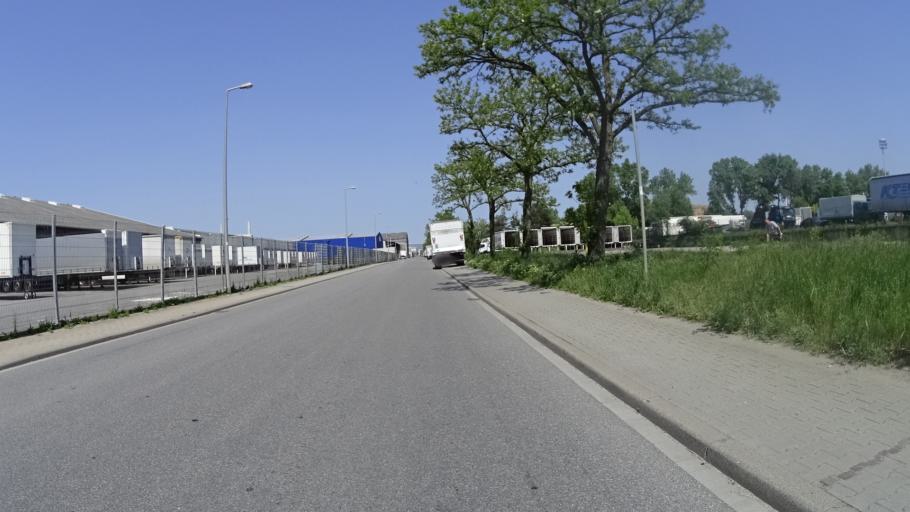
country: DE
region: Rheinland-Pfalz
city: Altrip
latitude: 49.4235
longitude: 8.5192
